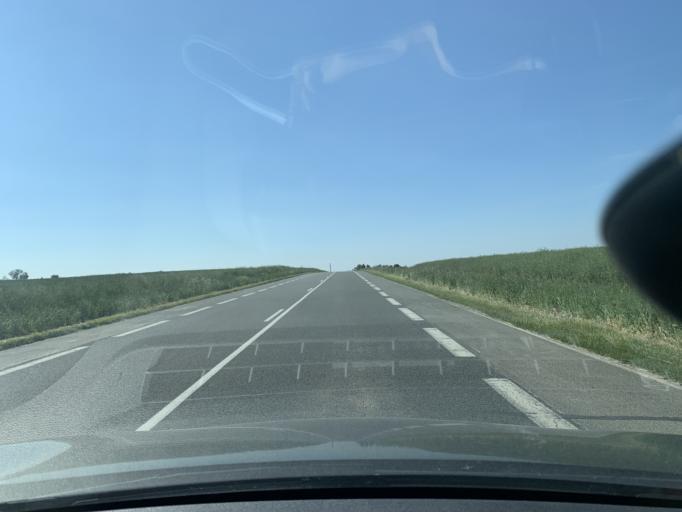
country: FR
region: Nord-Pas-de-Calais
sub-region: Departement du Nord
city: Cambrai
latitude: 50.1442
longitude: 3.2443
